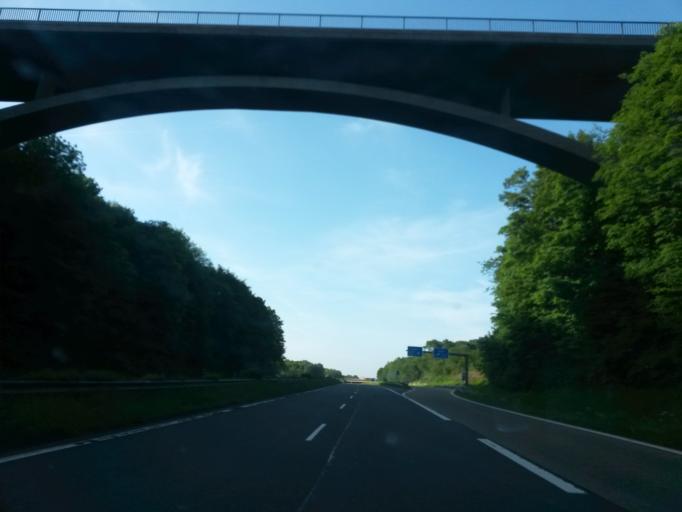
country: DE
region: North Rhine-Westphalia
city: Bergneustadt
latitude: 50.9708
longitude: 7.6419
